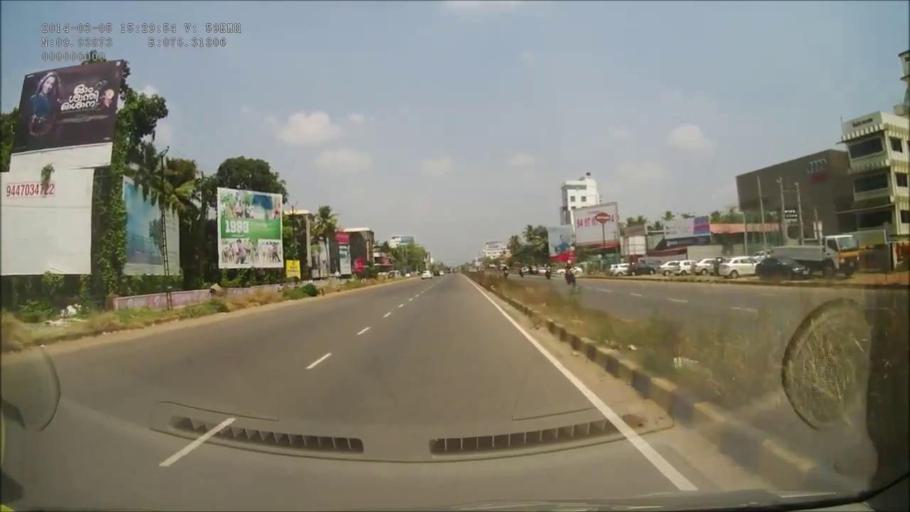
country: IN
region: Kerala
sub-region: Ernakulam
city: Cochin
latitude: 9.9402
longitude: 76.3180
